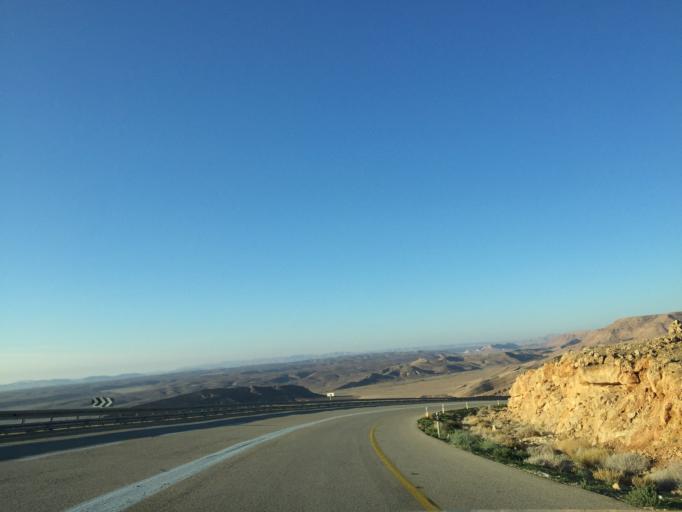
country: IL
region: Southern District
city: Mitzpe Ramon
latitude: 30.4957
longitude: 34.9362
